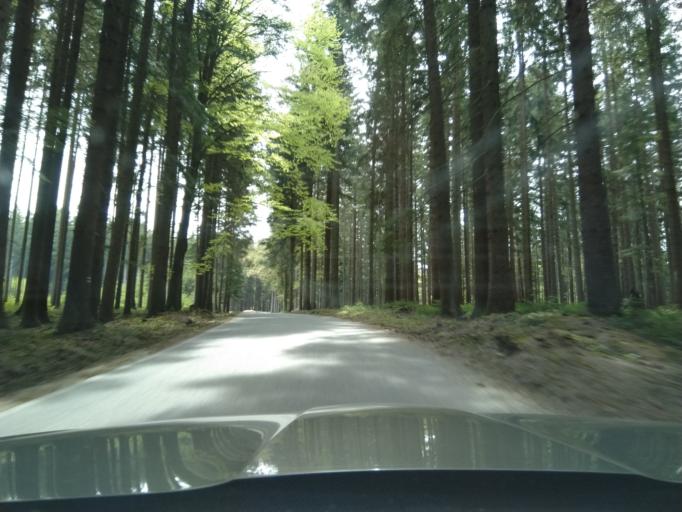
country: CZ
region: Jihocesky
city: Vacov
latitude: 49.1591
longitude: 13.6898
